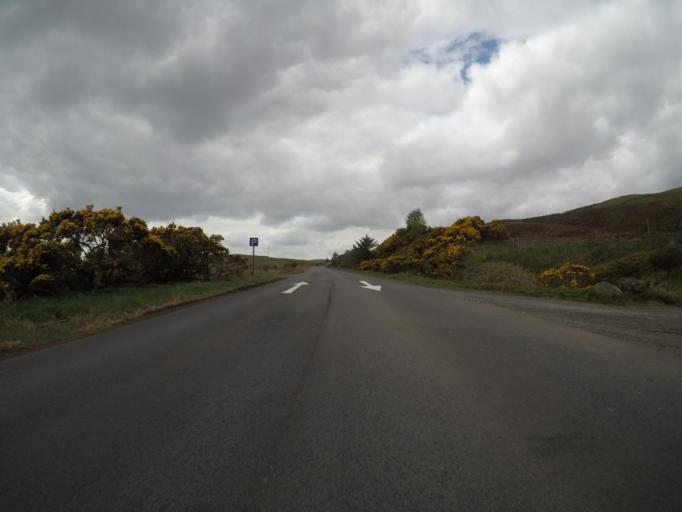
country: GB
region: Scotland
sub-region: Highland
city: Isle of Skye
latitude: 57.3291
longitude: -6.3350
